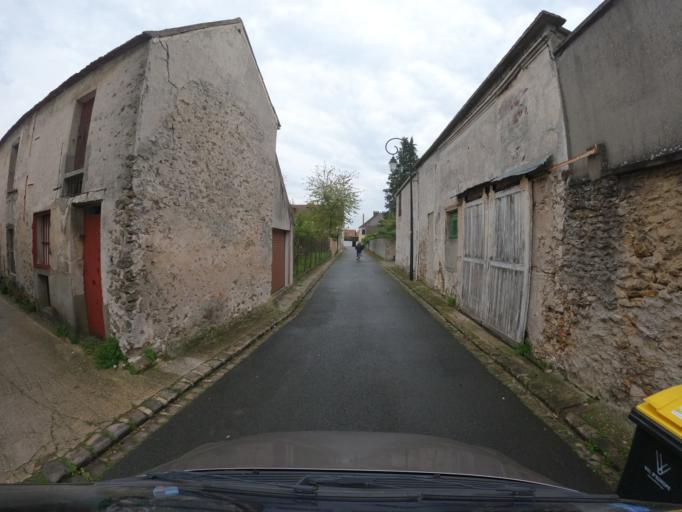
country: FR
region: Ile-de-France
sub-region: Departement de Seine-et-Marne
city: Villeneuve-le-Comte
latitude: 48.8149
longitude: 2.8291
